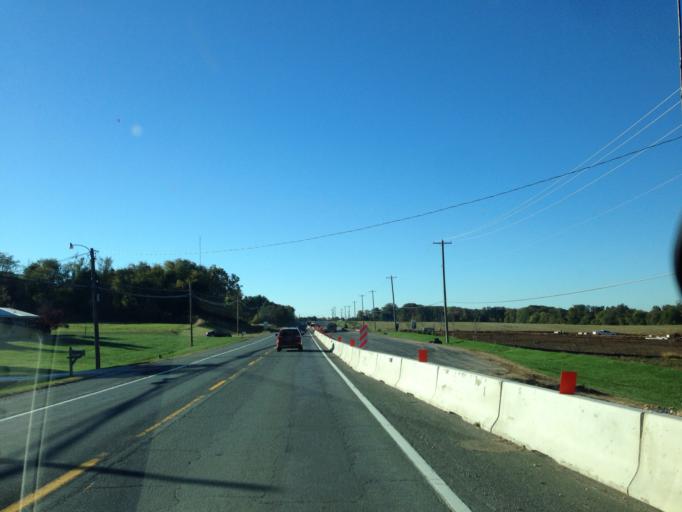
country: US
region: Maryland
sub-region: Montgomery County
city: Clarksburg
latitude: 39.2179
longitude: -77.2388
